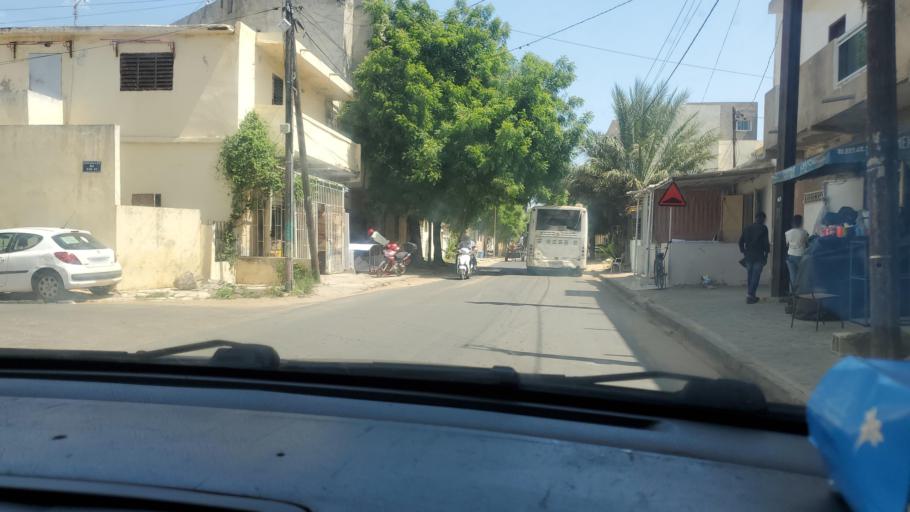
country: SN
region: Dakar
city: Grand Dakar
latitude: 14.7043
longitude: -17.4602
